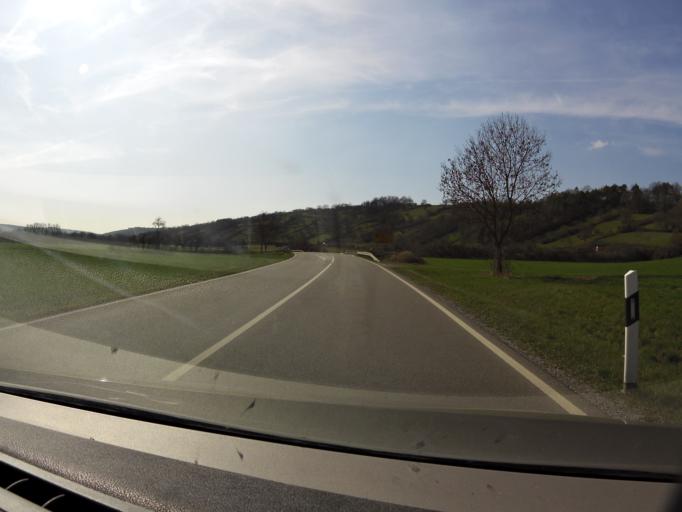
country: DE
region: Bavaria
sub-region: Regierungsbezirk Unterfranken
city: Bieberehren
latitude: 49.5219
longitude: 9.9957
